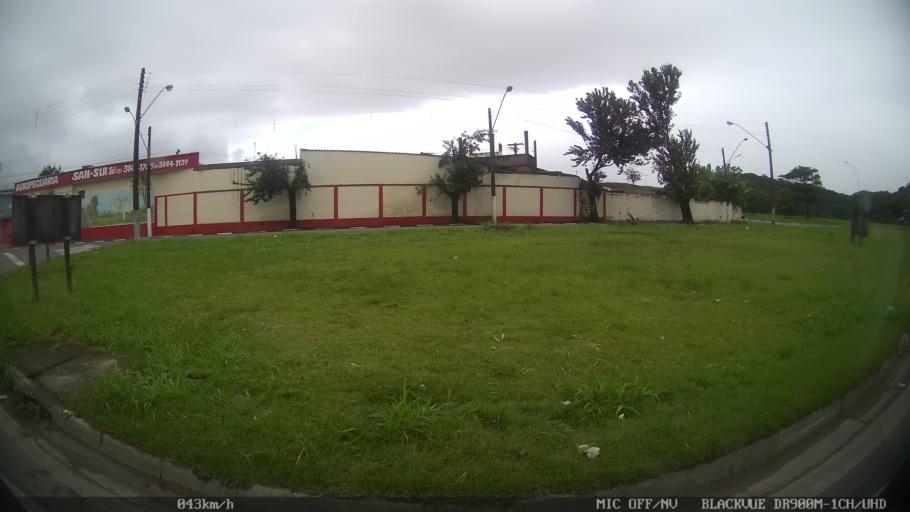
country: BR
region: Sao Paulo
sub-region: Juquia
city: Juquia
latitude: -24.3302
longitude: -47.6321
